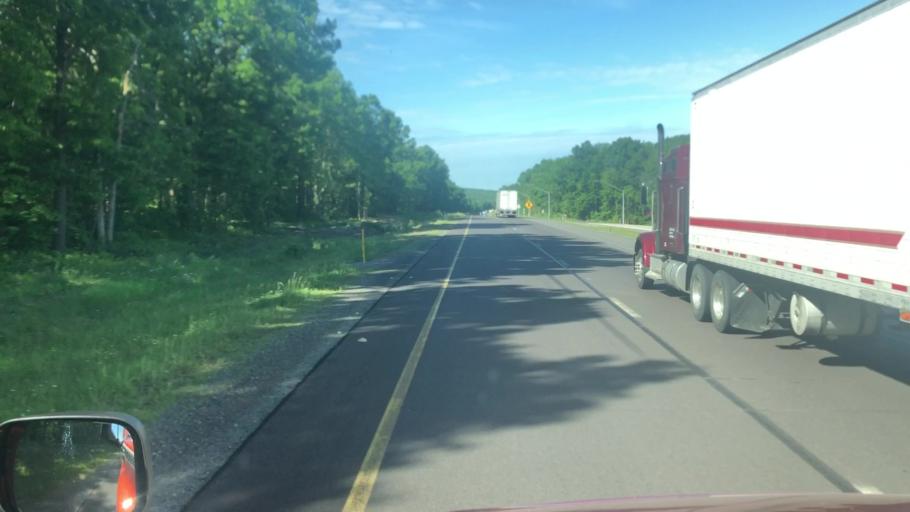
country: US
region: Pennsylvania
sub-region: Centre County
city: Milesburg
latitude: 41.0187
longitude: -77.9530
